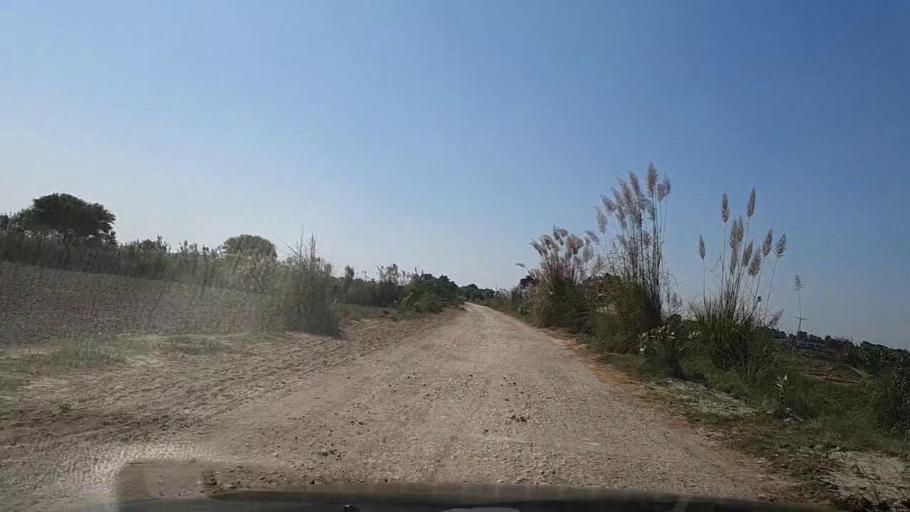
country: PK
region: Sindh
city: Mirpur Sakro
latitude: 24.6124
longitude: 67.7746
